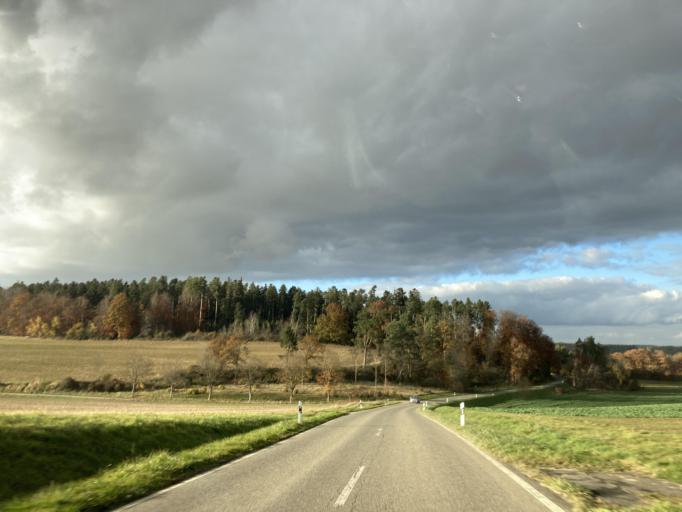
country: DE
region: Baden-Wuerttemberg
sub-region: Karlsruhe Region
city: Empfingen
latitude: 48.4067
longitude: 8.7511
